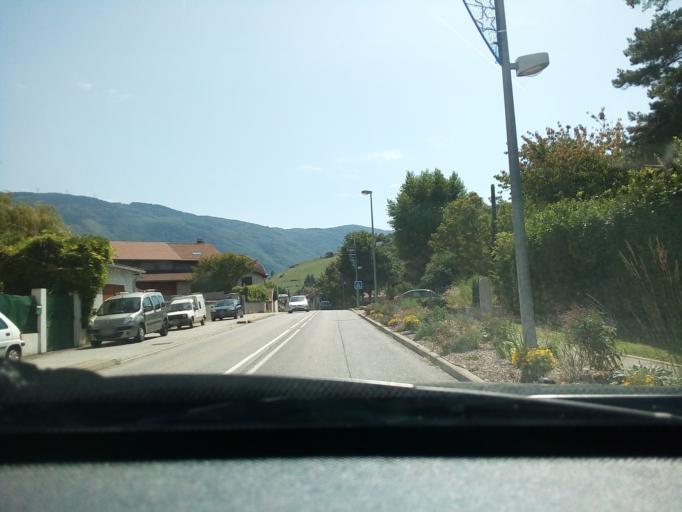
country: FR
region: Rhone-Alpes
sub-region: Departement de l'Isere
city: Brie-et-Angonnes
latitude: 45.1132
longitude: 5.7850
